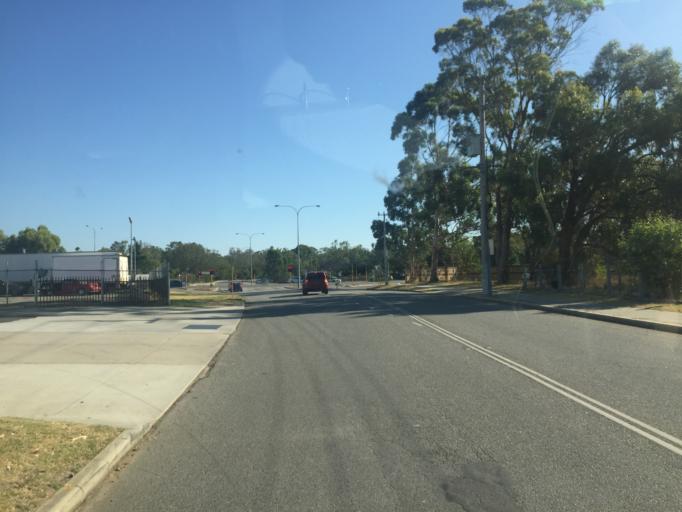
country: AU
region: Western Australia
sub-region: Gosnells
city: Kenwick
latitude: -32.0403
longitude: 115.9673
